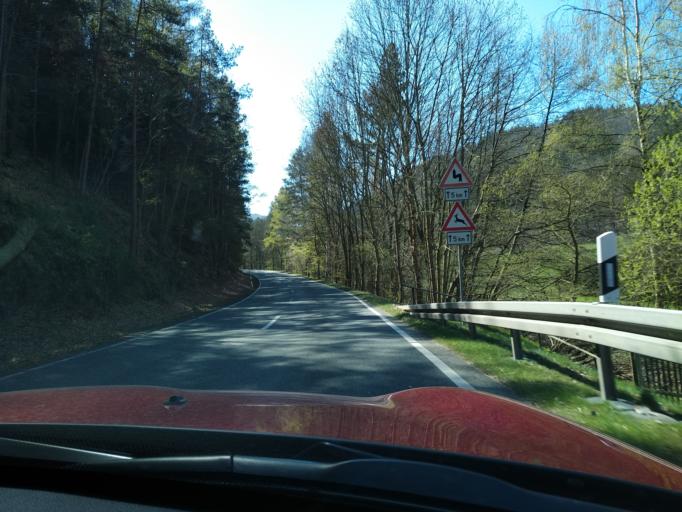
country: DE
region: Thuringia
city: Bad Blankenburg
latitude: 50.6605
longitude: 11.2892
